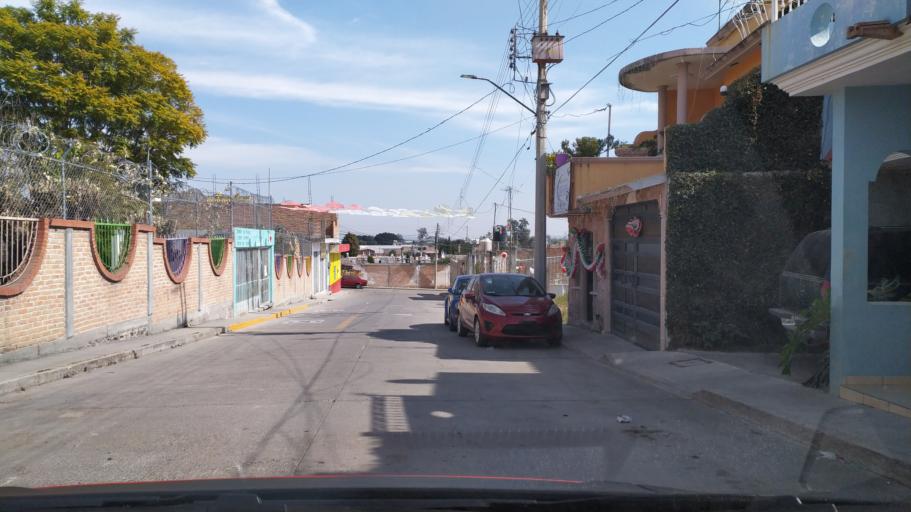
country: MX
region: Guanajuato
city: Ciudad Manuel Doblado
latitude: 20.7331
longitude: -101.9546
